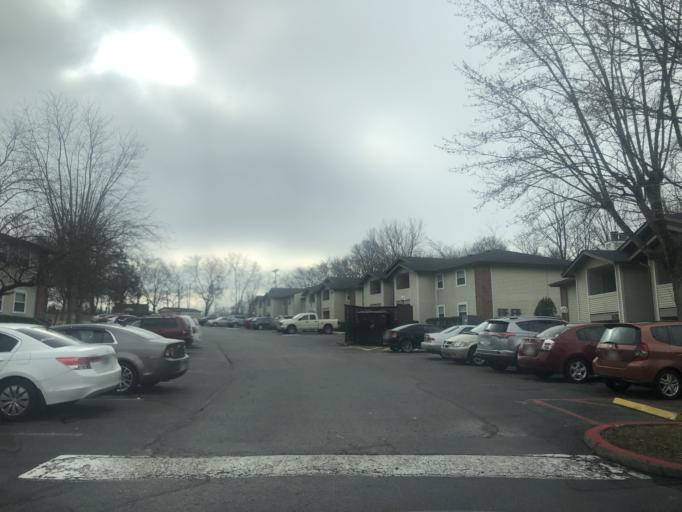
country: US
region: Tennessee
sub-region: Rutherford County
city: La Vergne
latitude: 36.0685
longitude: -86.6438
